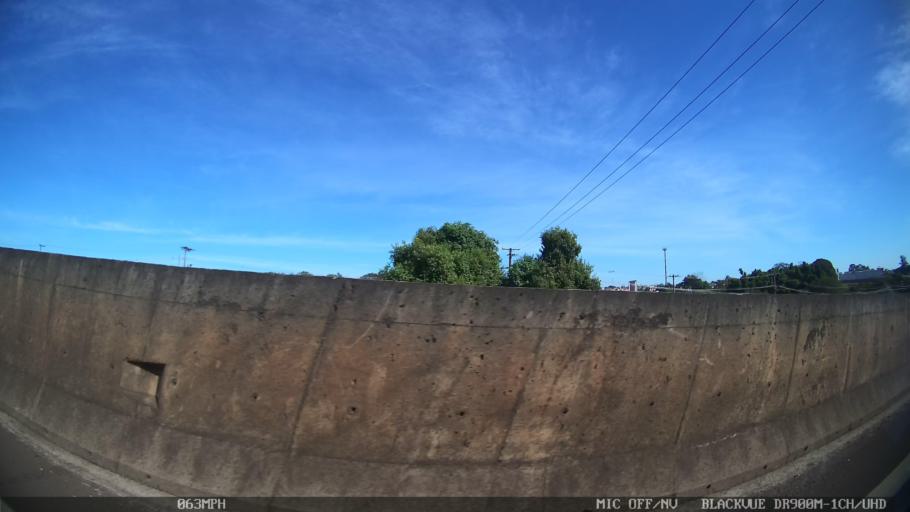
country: BR
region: Sao Paulo
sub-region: Leme
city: Leme
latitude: -22.1946
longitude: -47.3971
